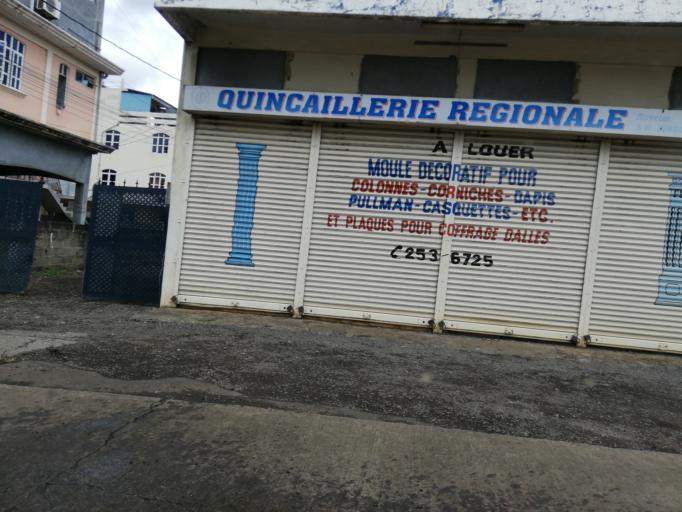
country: MU
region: Pamplemousses
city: Morcellemont Saint Andre
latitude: -20.0670
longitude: 57.5497
